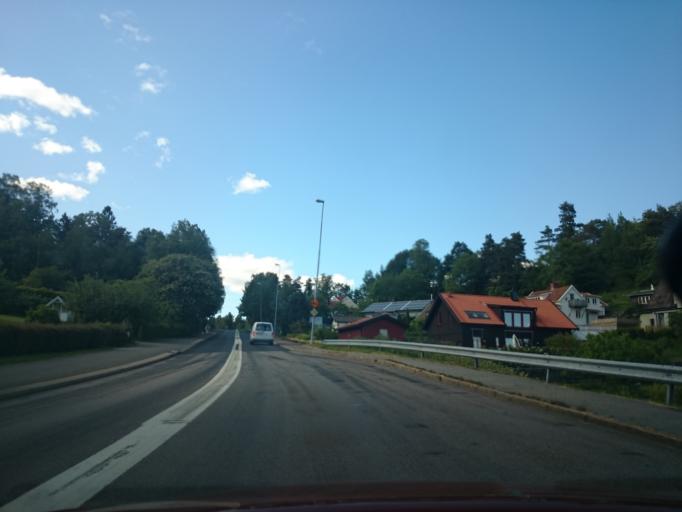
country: SE
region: Vaestra Goetaland
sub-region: Molndal
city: Moelndal
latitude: 57.6673
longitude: 12.0580
